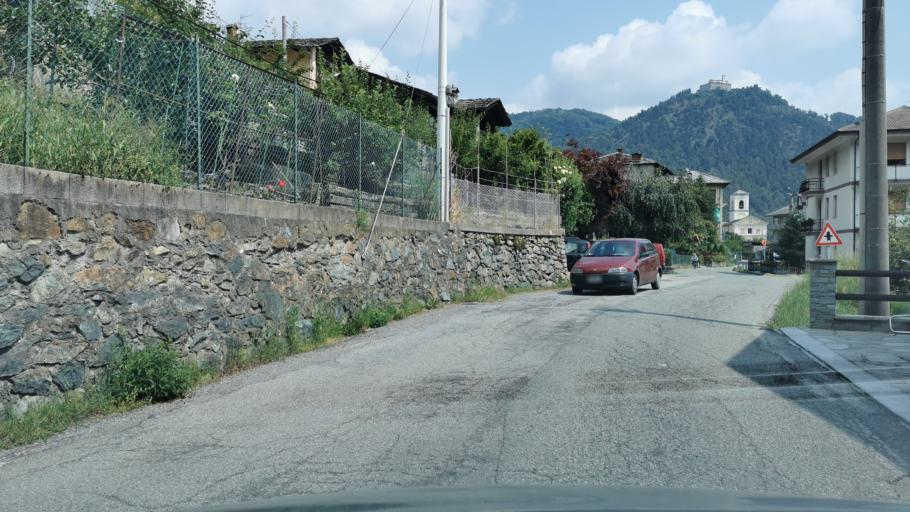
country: IT
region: Piedmont
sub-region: Provincia di Torino
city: Traves
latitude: 45.2691
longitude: 7.4280
